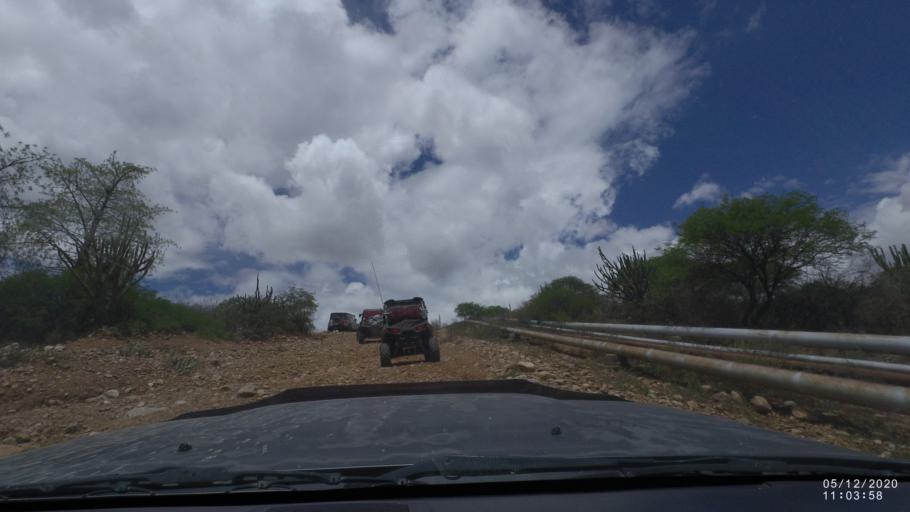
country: BO
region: Cochabamba
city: Sipe Sipe
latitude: -17.5495
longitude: -66.3016
